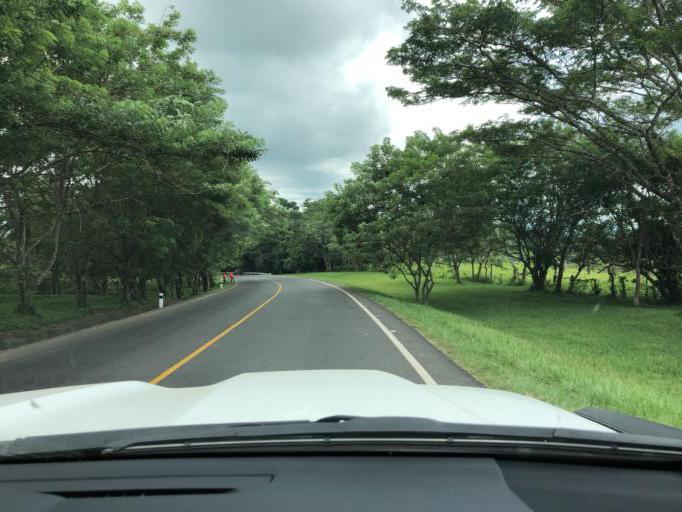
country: NI
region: Chontales
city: Santo Tomas
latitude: 12.0590
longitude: -85.0586
